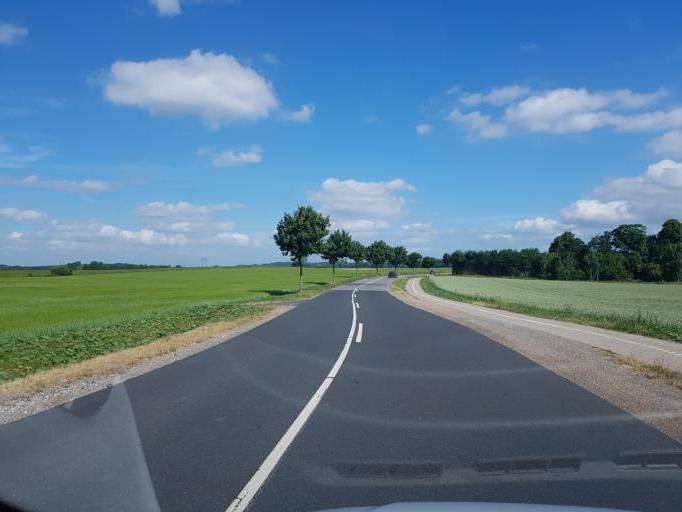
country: DK
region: Zealand
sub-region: Lejre Kommune
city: Osted
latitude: 55.5733
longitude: 11.9674
